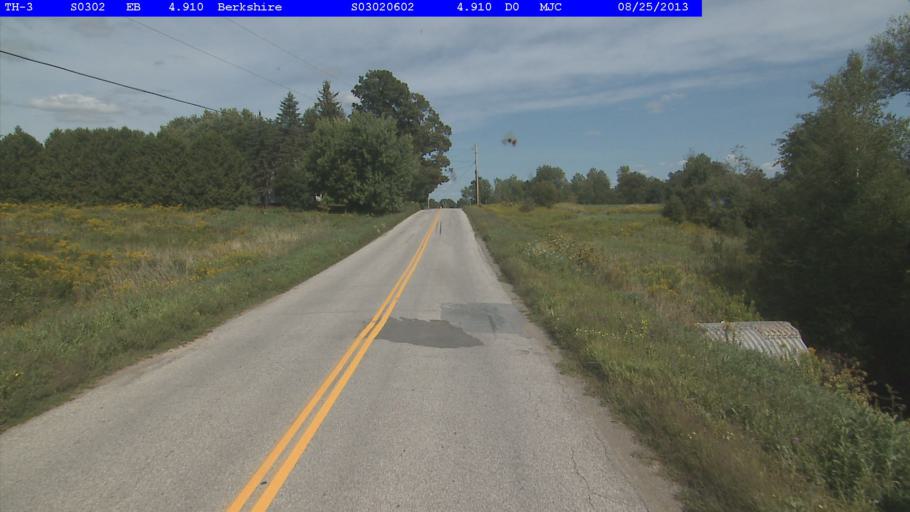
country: US
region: Vermont
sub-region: Franklin County
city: Richford
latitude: 44.9817
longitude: -72.7224
